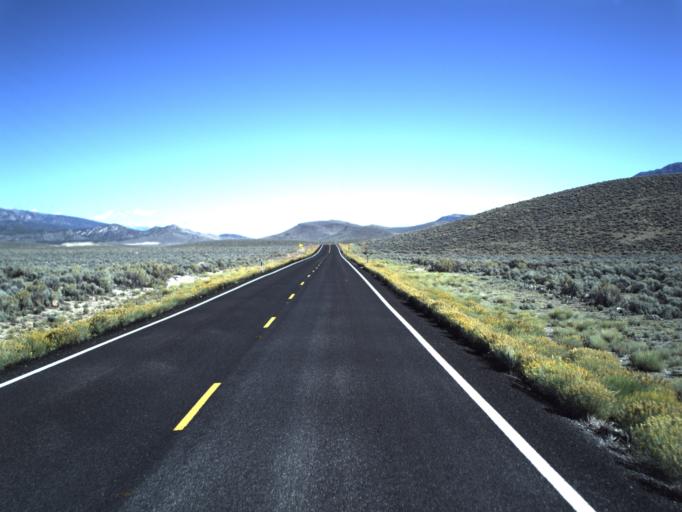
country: US
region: Utah
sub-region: Piute County
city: Junction
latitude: 38.2258
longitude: -111.9975
